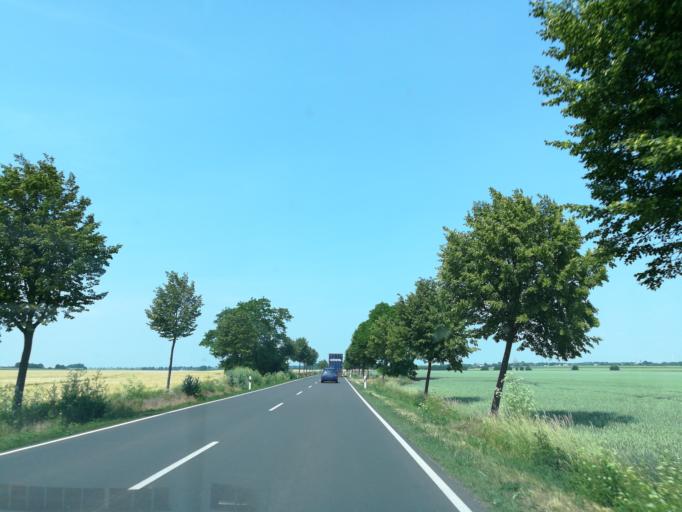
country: DE
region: Saxony-Anhalt
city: Schneidlingen
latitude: 51.9116
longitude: 11.4292
